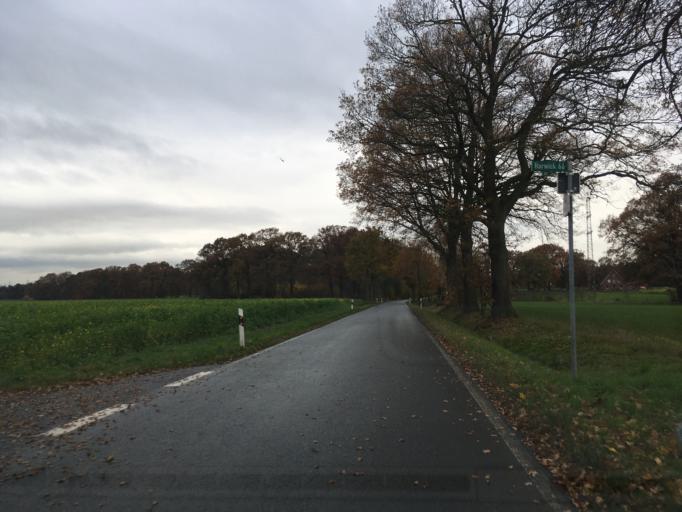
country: DE
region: North Rhine-Westphalia
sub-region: Regierungsbezirk Munster
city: Gescher
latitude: 51.9763
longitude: 7.0060
